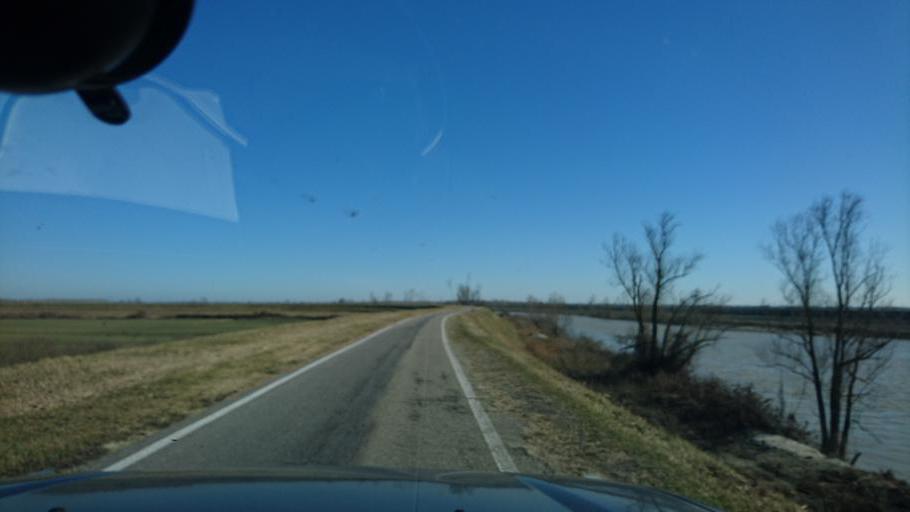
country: IT
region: Veneto
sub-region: Provincia di Rovigo
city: Ariano
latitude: 44.9316
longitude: 12.1521
